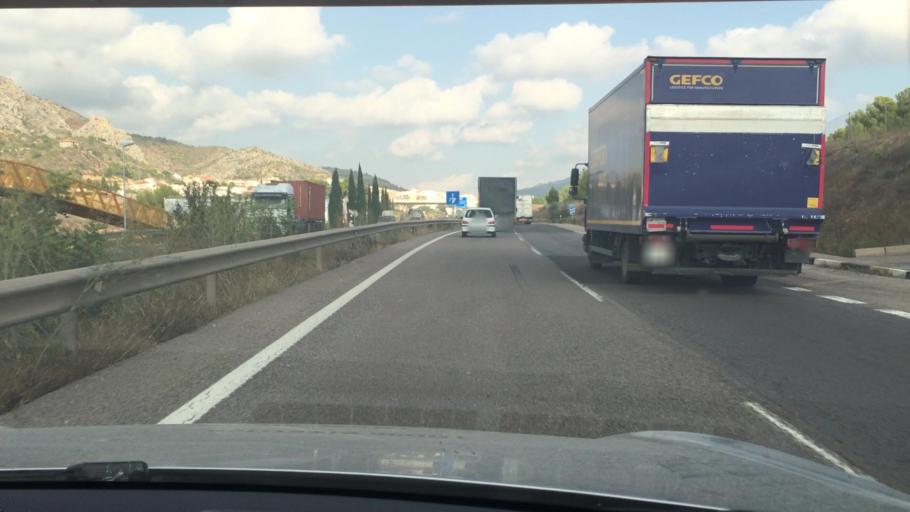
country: ES
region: Valencia
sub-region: Provincia de Castello
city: Borriol
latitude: 40.0319
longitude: -0.0830
